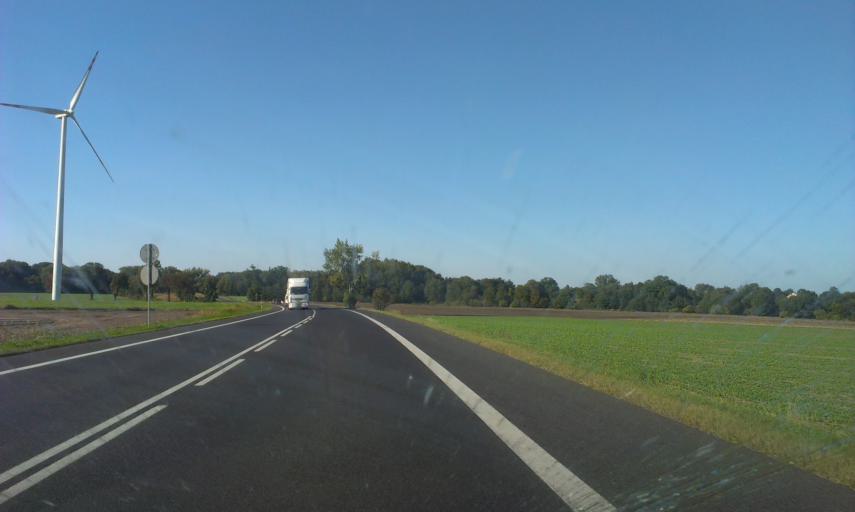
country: PL
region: Kujawsko-Pomorskie
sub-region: Powiat torunski
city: Chelmza
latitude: 53.2025
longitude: 18.5656
